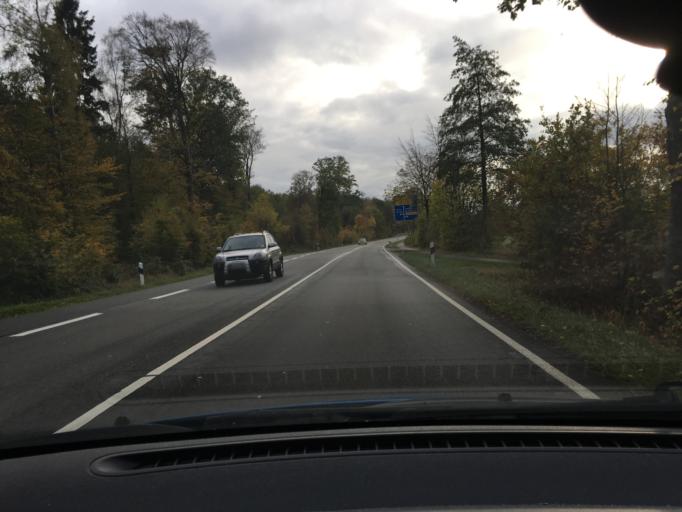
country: DE
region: Schleswig-Holstein
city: Talkau
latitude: 53.5662
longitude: 10.5630
